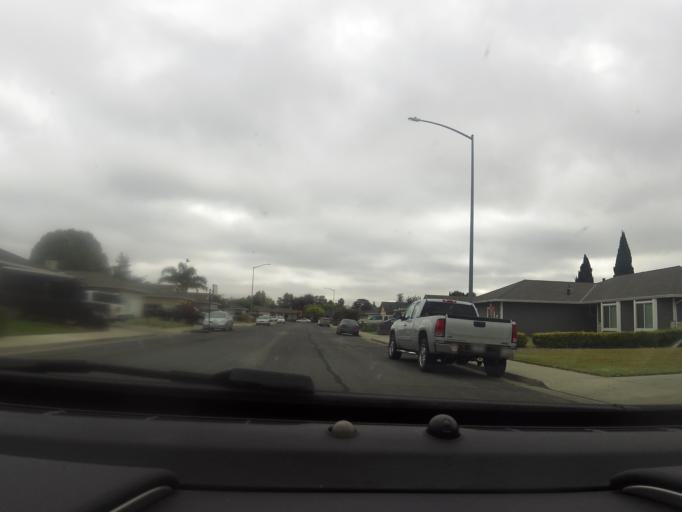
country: US
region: California
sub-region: San Benito County
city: Hollister
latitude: 36.8426
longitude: -121.4106
